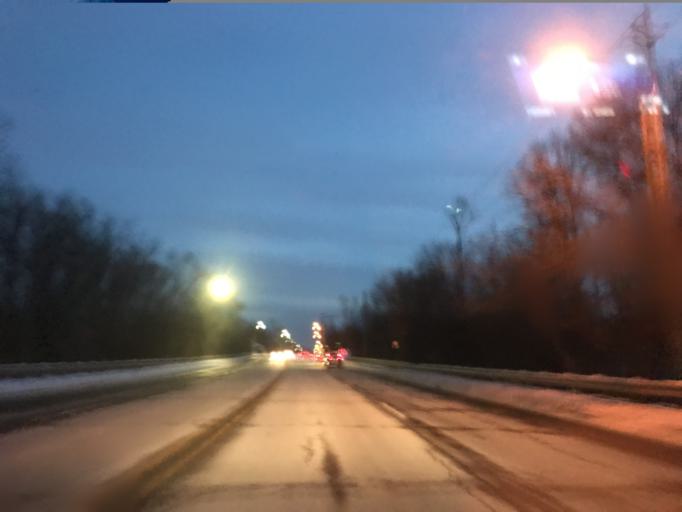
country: US
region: Michigan
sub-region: Wayne County
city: Redford
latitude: 42.4054
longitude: -83.3153
